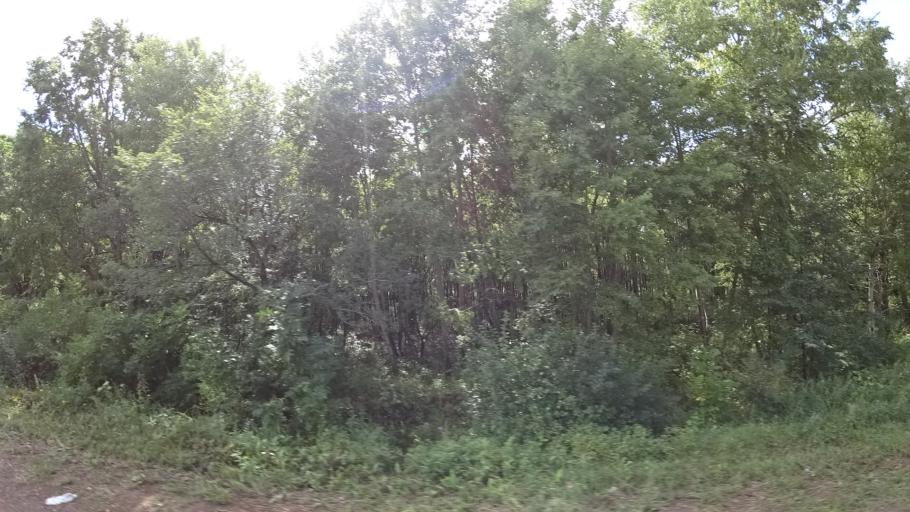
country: RU
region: Primorskiy
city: Lyalichi
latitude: 44.1451
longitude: 132.4009
